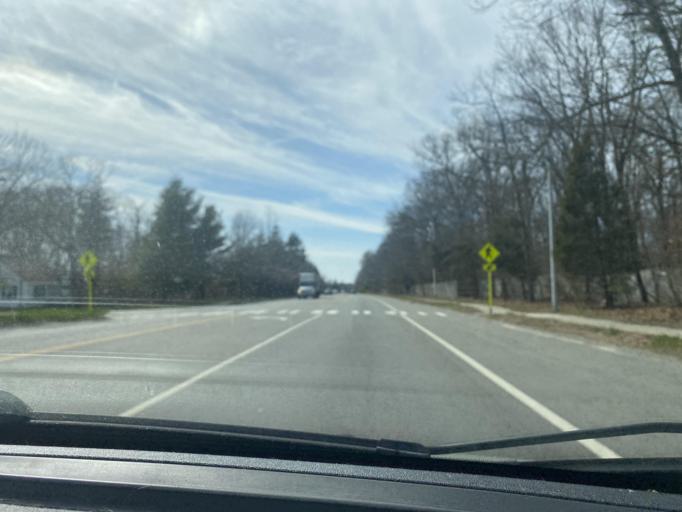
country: US
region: New York
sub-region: Suffolk County
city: East Shoreham
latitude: 40.9454
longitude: -72.8846
